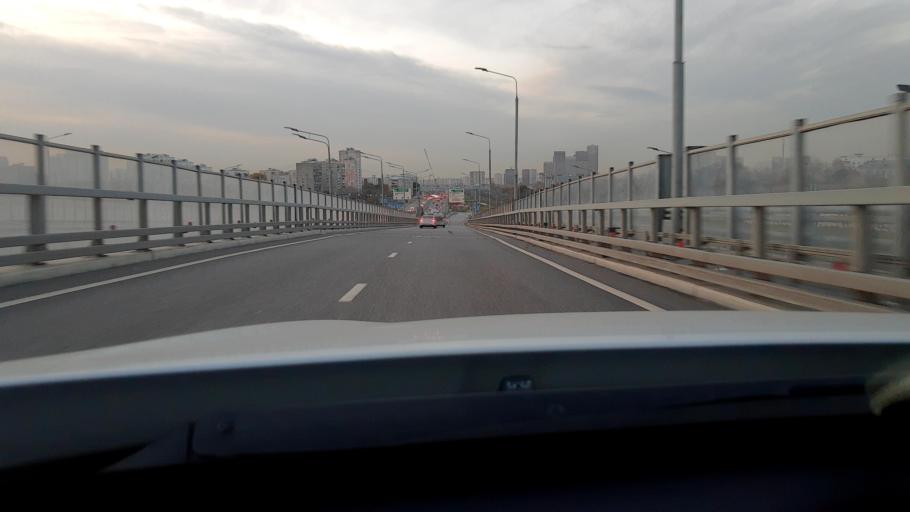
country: RU
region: Moscow
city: Likhobory
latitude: 55.8396
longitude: 37.5661
